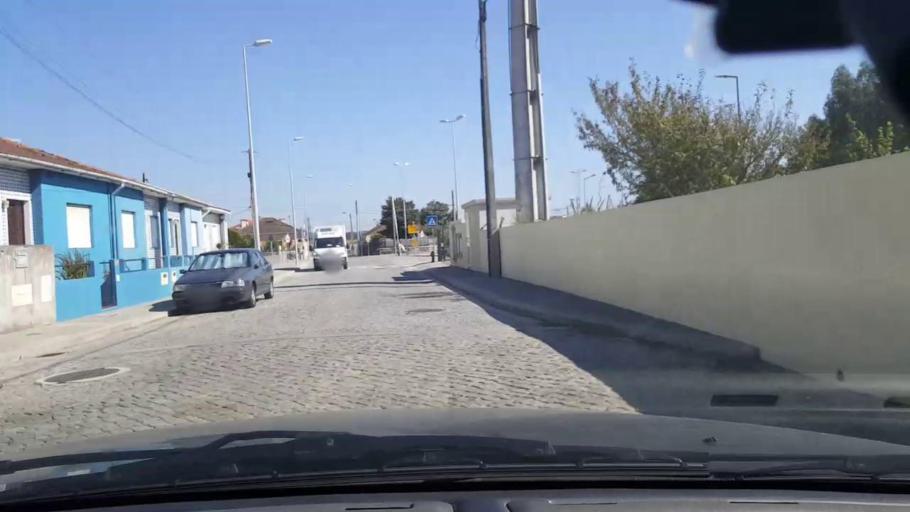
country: PT
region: Porto
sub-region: Matosinhos
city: Lavra
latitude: 41.2945
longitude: -8.7007
